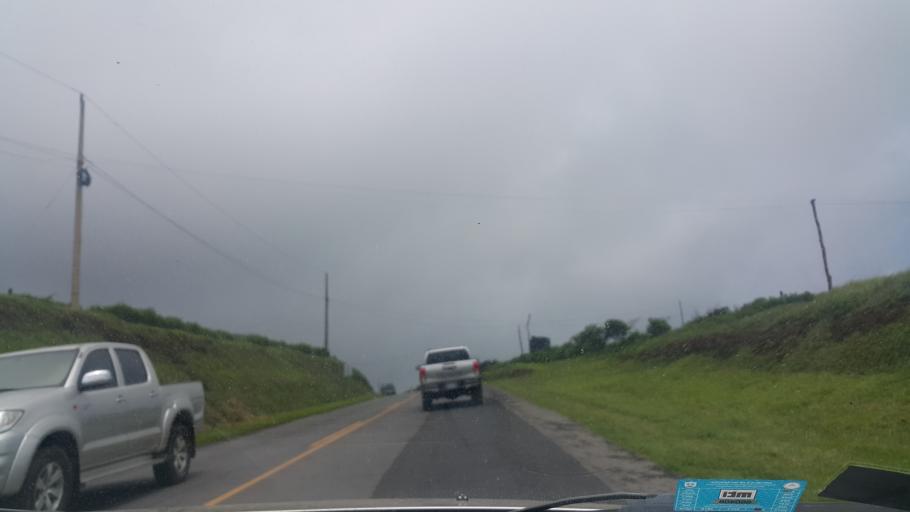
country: NI
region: Managua
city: El Crucero
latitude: 11.9403
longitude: -86.2967
